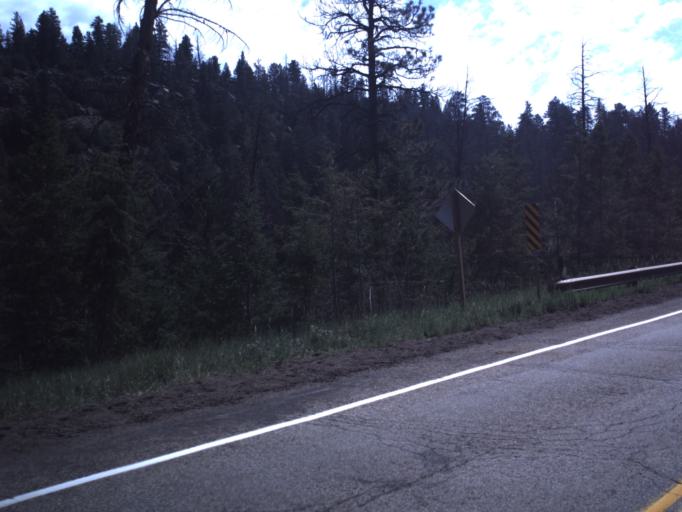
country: US
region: Utah
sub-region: Daggett County
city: Manila
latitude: 40.8707
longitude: -109.6905
